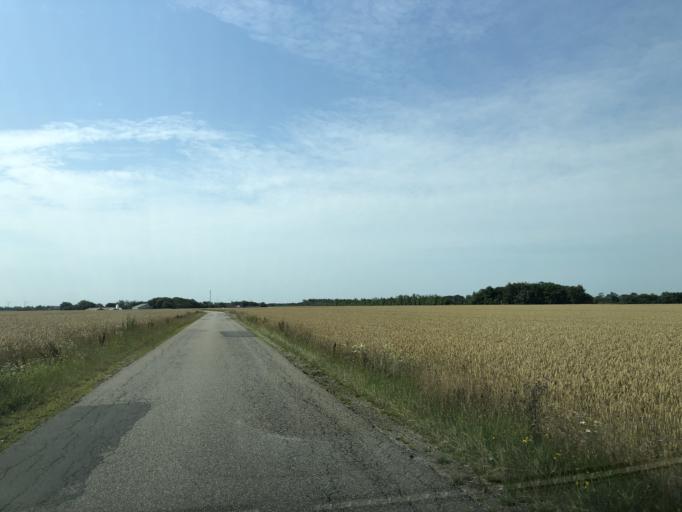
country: DK
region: Central Jutland
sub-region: Lemvig Kommune
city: Lemvig
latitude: 56.4449
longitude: 8.2906
